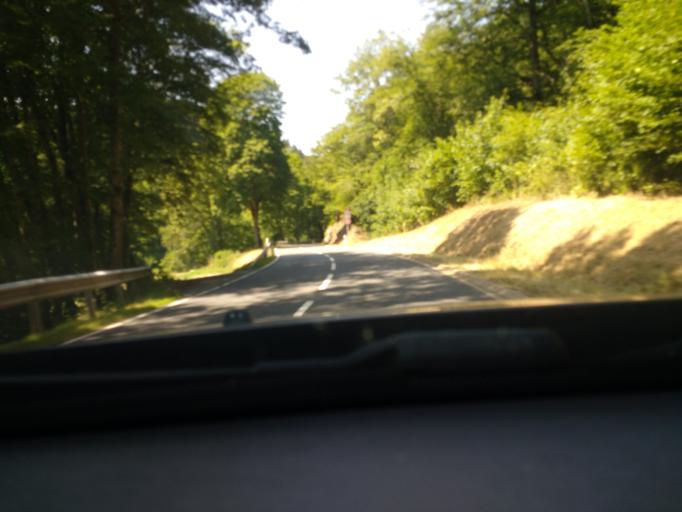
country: DE
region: Rheinland-Pfalz
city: Manderscheid
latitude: 50.0957
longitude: 6.7915
